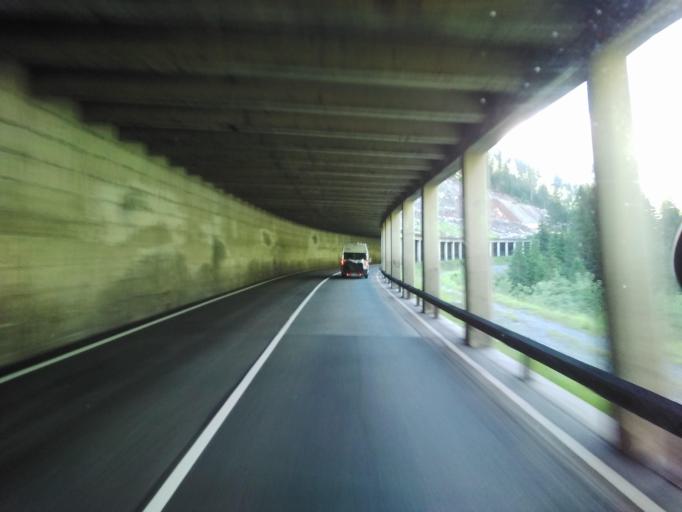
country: AT
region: Salzburg
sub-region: Politischer Bezirk Zell am See
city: Stuhlfelden
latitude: 47.1778
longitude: 12.5317
